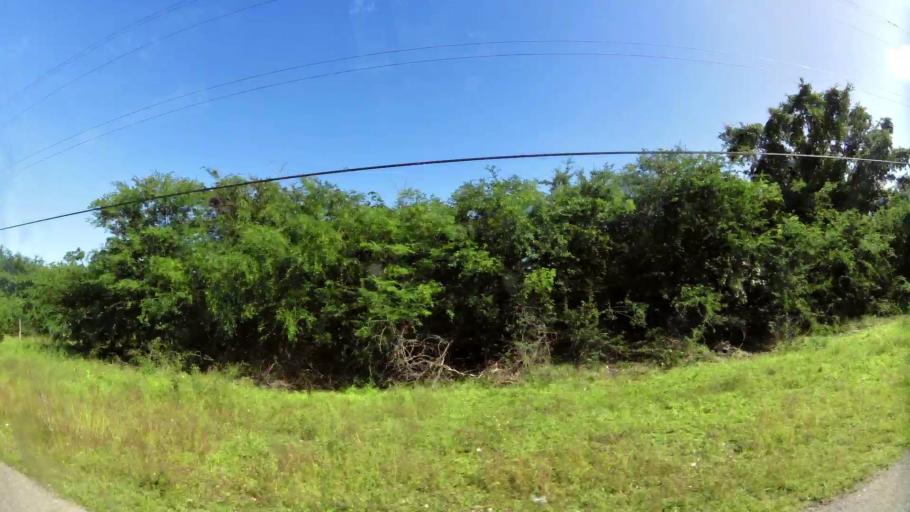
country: AG
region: Barbuda
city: Codrington
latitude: 17.6129
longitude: -61.8284
